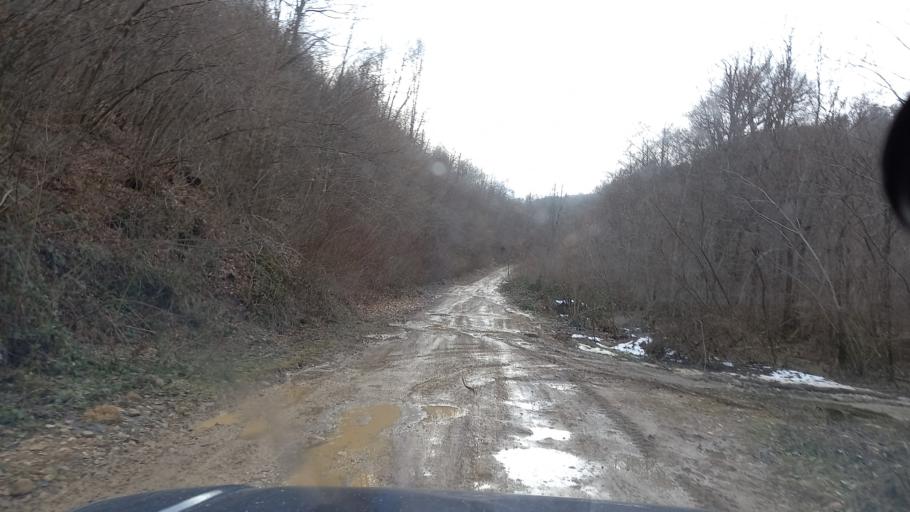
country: RU
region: Adygeya
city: Kamennomostskiy
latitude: 44.1737
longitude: 40.3001
